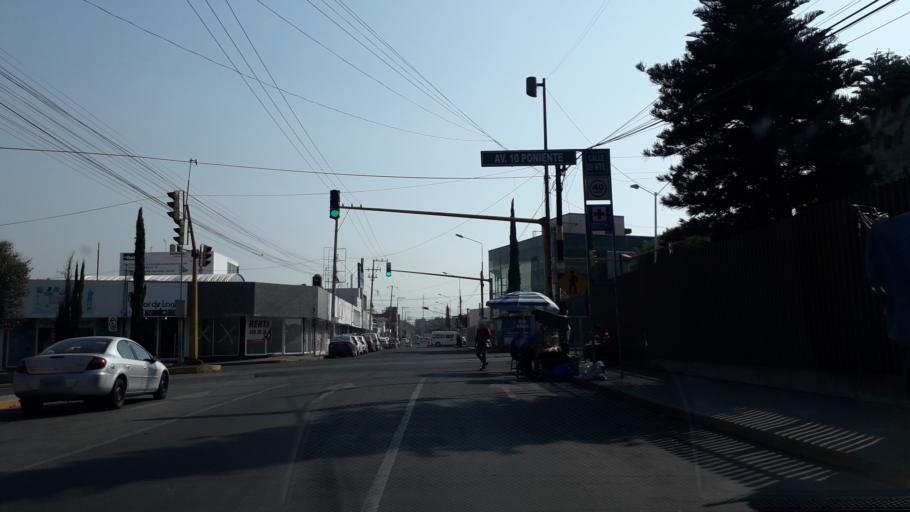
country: MX
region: Puebla
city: Puebla
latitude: 19.0585
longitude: -98.2172
